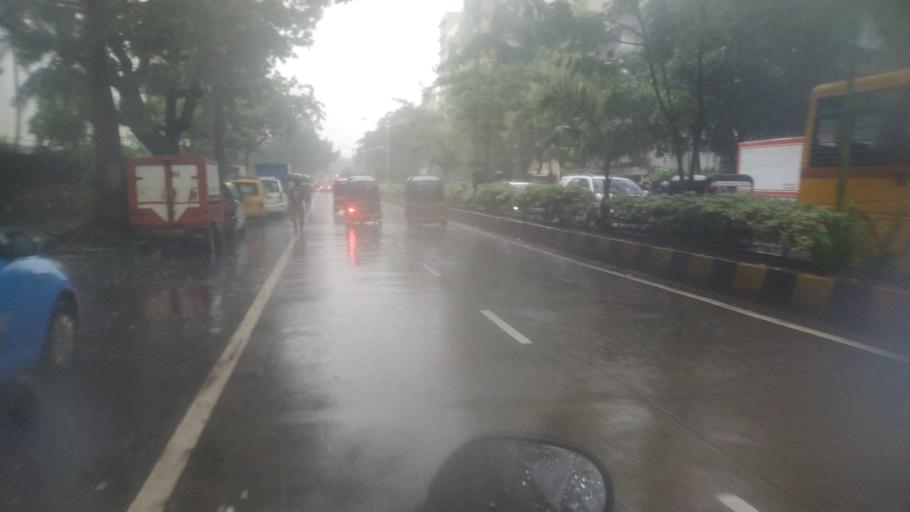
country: IN
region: Maharashtra
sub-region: Mumbai Suburban
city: Mumbai
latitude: 19.1033
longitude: 72.8341
